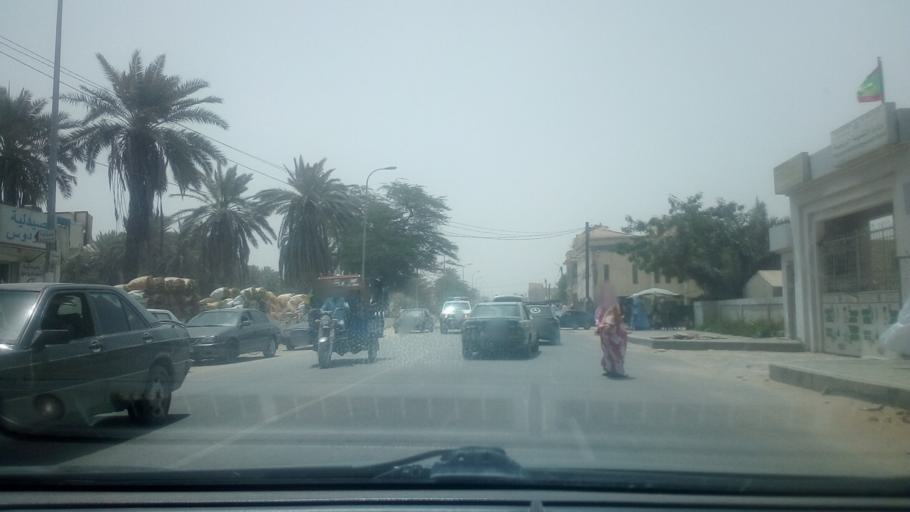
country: MR
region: Nouakchott
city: Nouakchott
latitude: 18.0835
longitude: -15.9903
